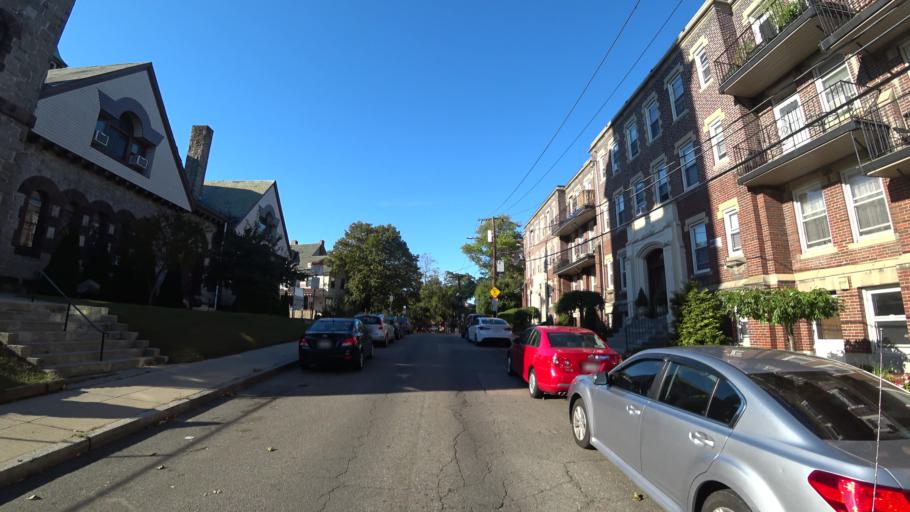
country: US
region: Massachusetts
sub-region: Norfolk County
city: Brookline
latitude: 42.3516
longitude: -71.1340
